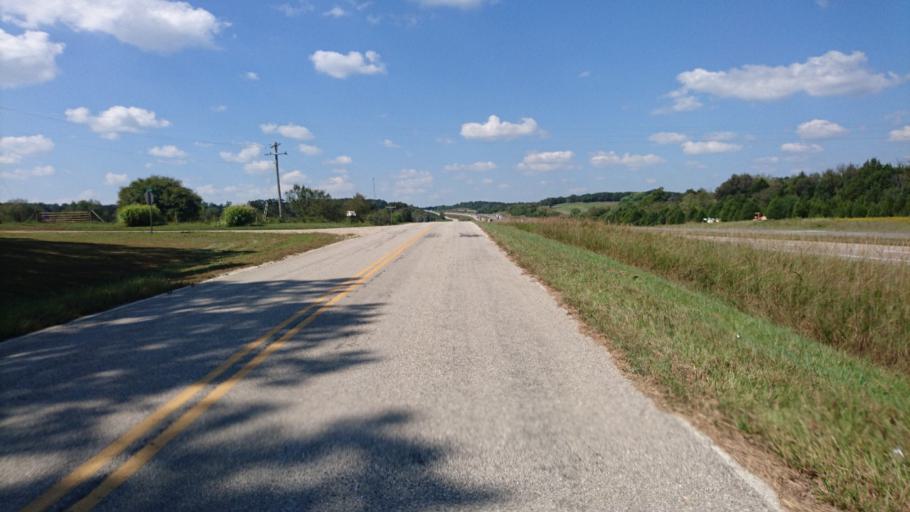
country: US
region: Missouri
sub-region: Pulaski County
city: Richland
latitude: 37.7575
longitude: -92.4624
